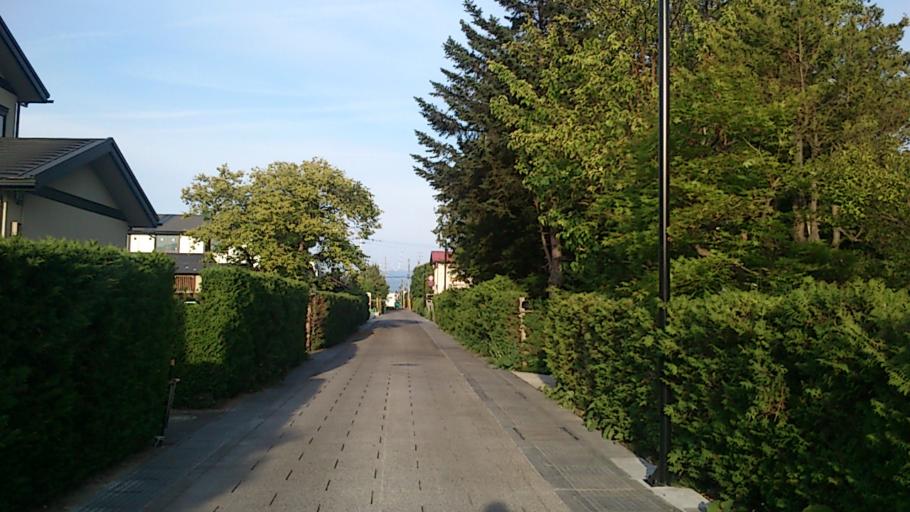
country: JP
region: Aomori
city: Hirosaki
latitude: 40.6131
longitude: 140.4652
